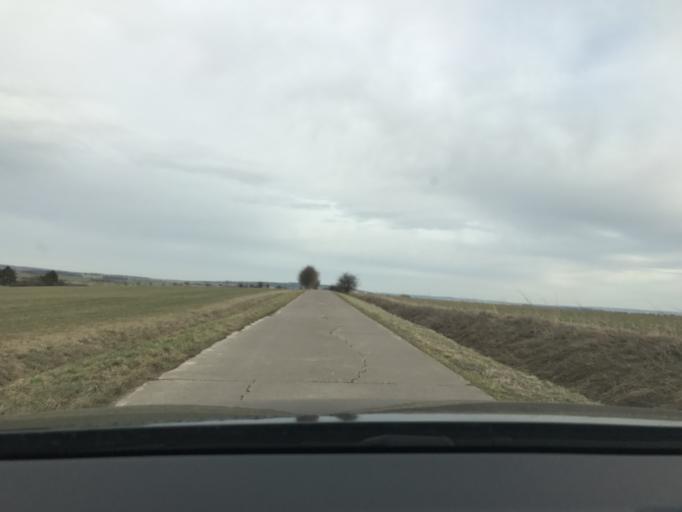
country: DE
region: Thuringia
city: Anrode
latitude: 51.2504
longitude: 10.3921
